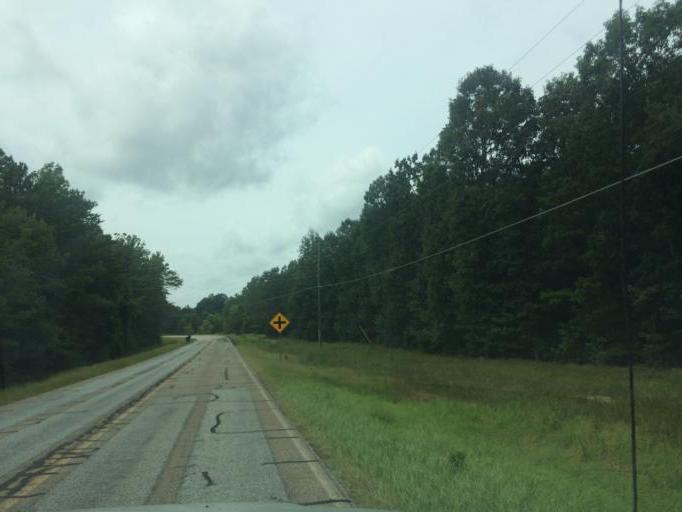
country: US
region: Georgia
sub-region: Hart County
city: Hartwell
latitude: 34.2865
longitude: -82.8573
